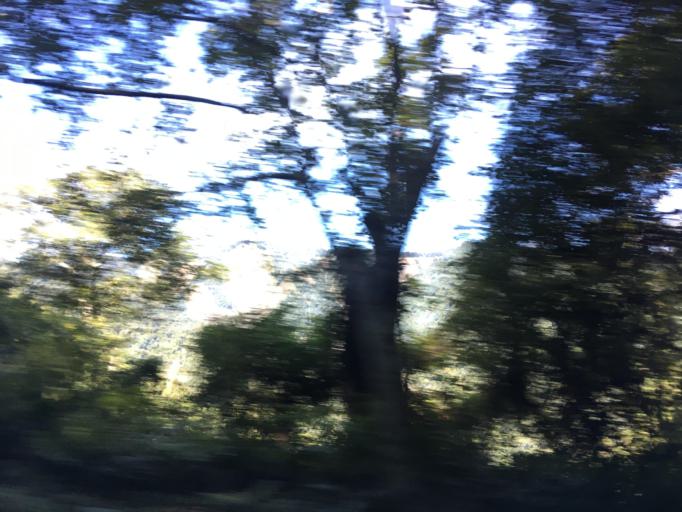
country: TW
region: Taiwan
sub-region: Yilan
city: Yilan
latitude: 24.5460
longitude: 121.5128
